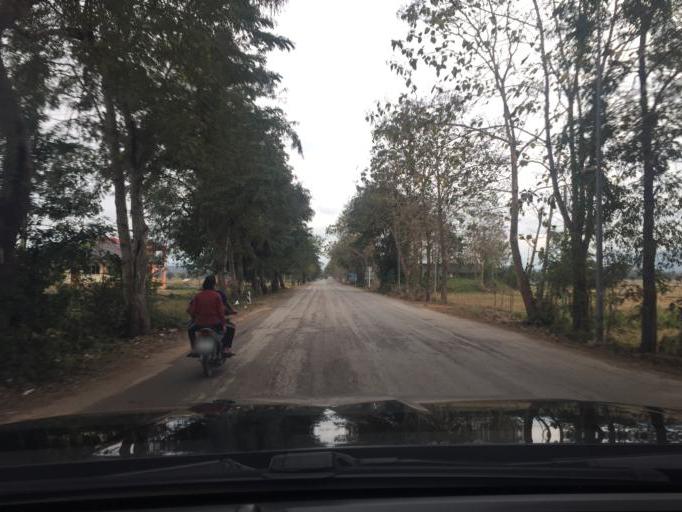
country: TH
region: Phayao
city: Pong
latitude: 19.1670
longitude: 100.2897
